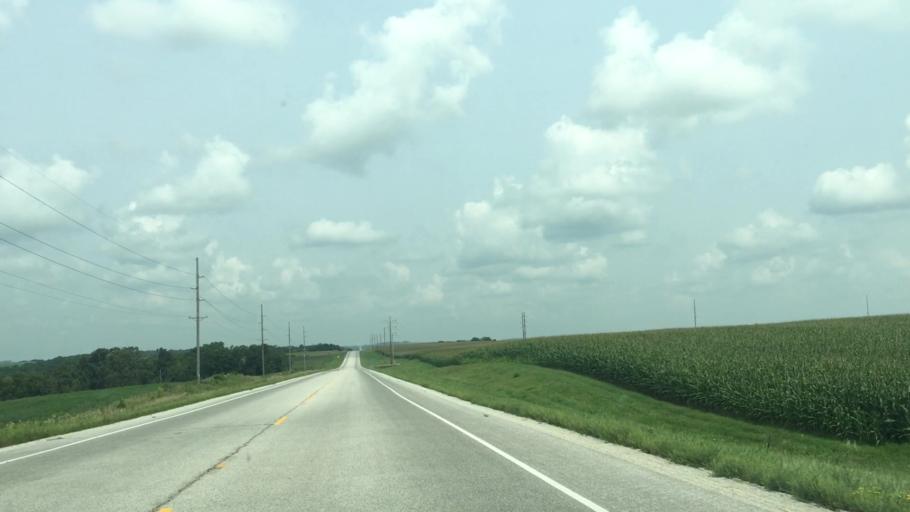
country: US
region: Minnesota
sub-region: Fillmore County
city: Harmony
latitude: 43.5624
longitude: -91.9297
